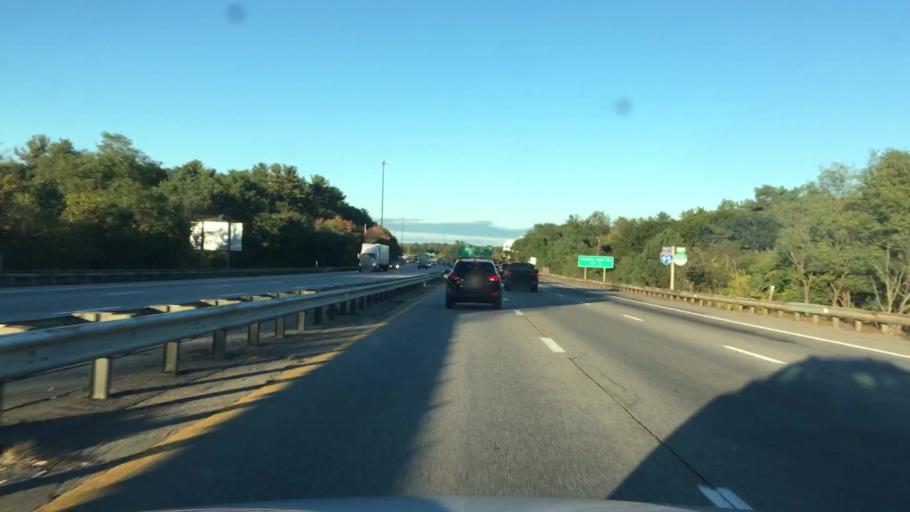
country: US
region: Maine
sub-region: York County
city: South Eliot
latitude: 43.0962
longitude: -70.7600
